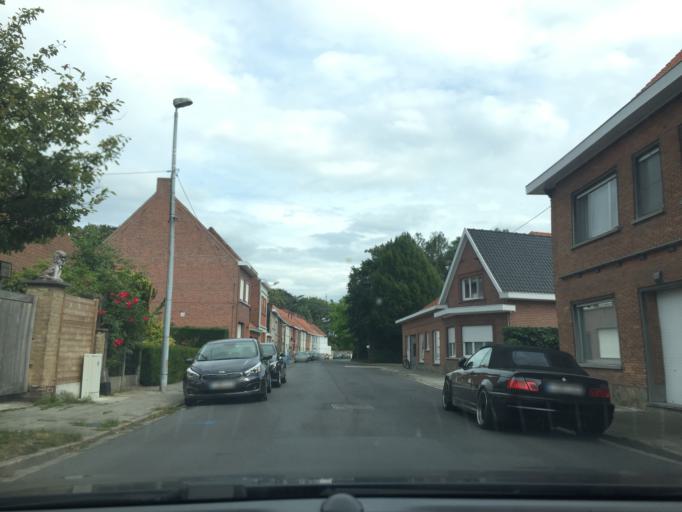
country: BE
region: Flanders
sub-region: Provincie West-Vlaanderen
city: Izegem
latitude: 50.9159
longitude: 3.2237
